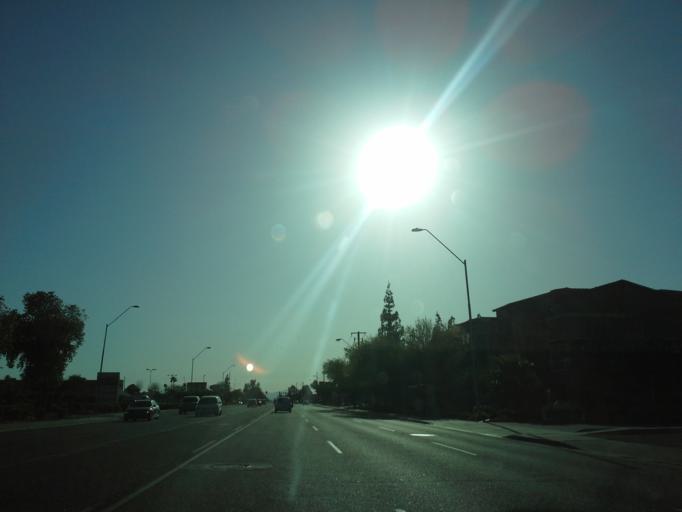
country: US
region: Arizona
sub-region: Maricopa County
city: Glendale
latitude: 33.6252
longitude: -112.1291
